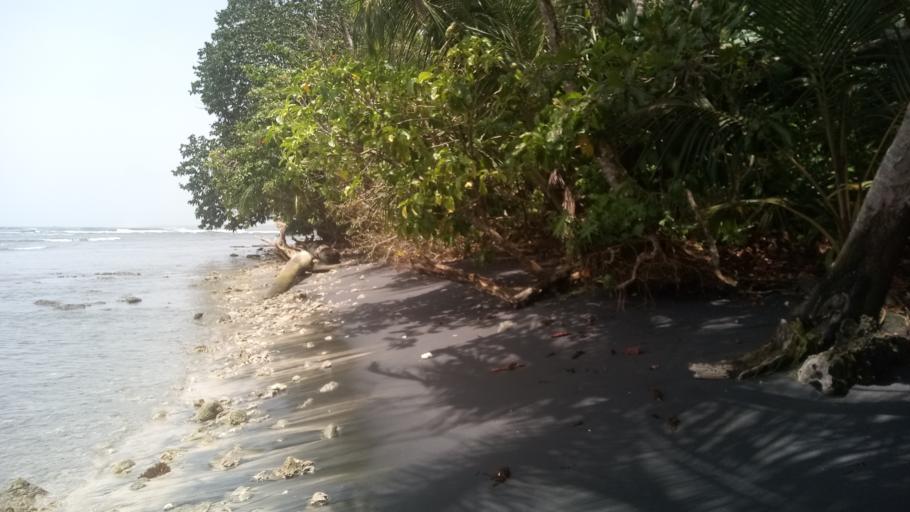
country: CR
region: Limon
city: Sixaola
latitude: 9.6254
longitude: -82.6198
